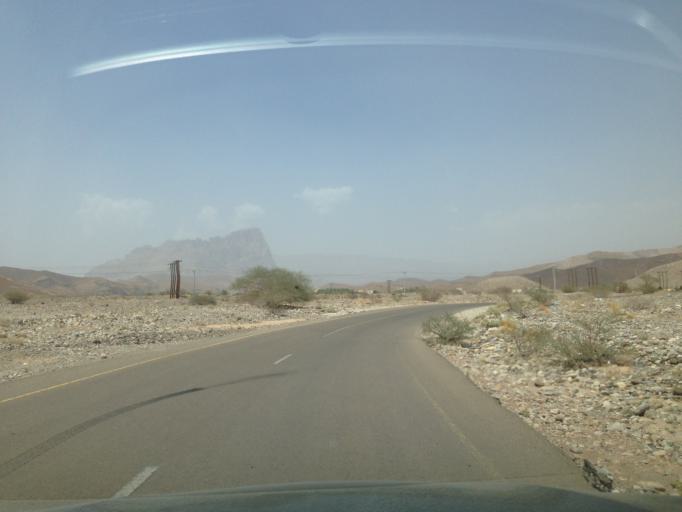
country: OM
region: Az Zahirah
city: `Ibri
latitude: 23.1759
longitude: 56.9107
